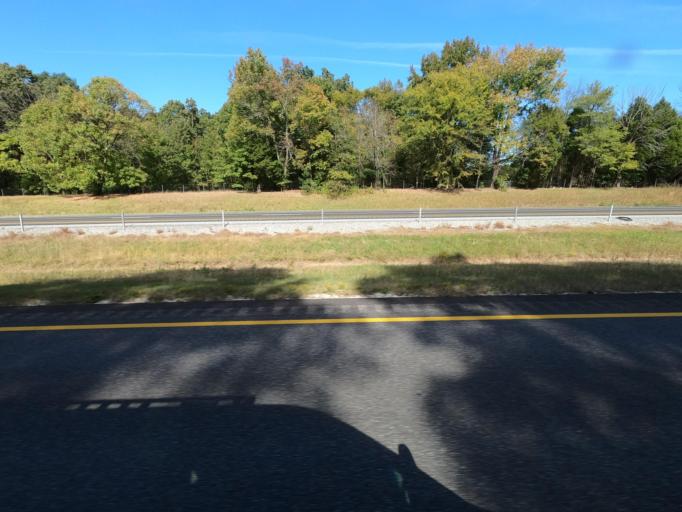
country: US
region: Tennessee
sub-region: Crockett County
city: Bells
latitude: 35.6201
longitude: -88.9901
